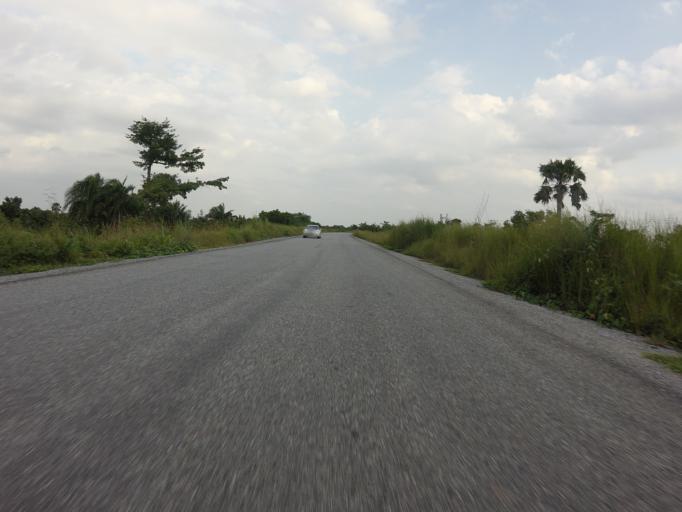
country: GH
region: Volta
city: Ho
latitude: 6.3830
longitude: 0.5305
